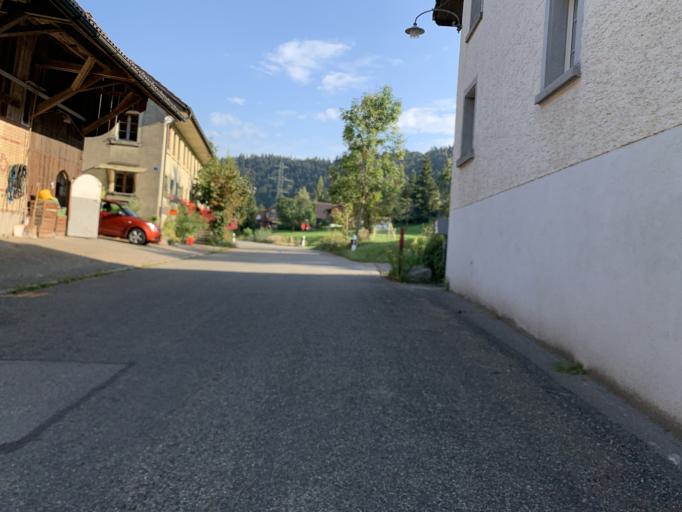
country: CH
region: Zurich
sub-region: Bezirk Hinwil
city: Baretswil
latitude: 47.3230
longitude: 8.8699
